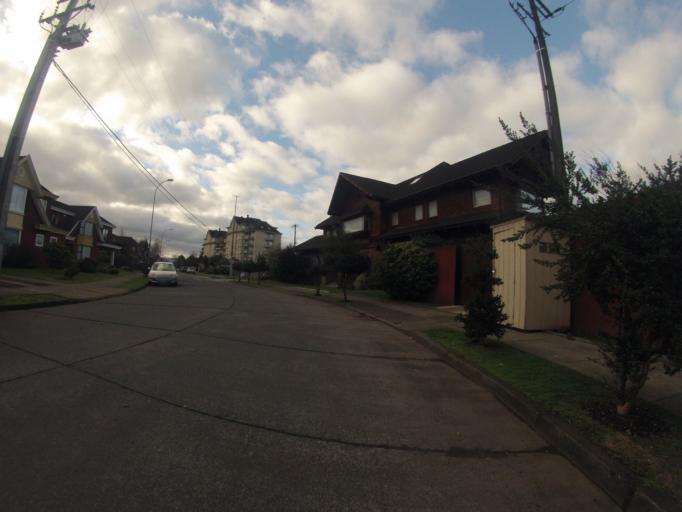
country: CL
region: Araucania
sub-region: Provincia de Cautin
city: Temuco
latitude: -38.7412
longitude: -72.6399
